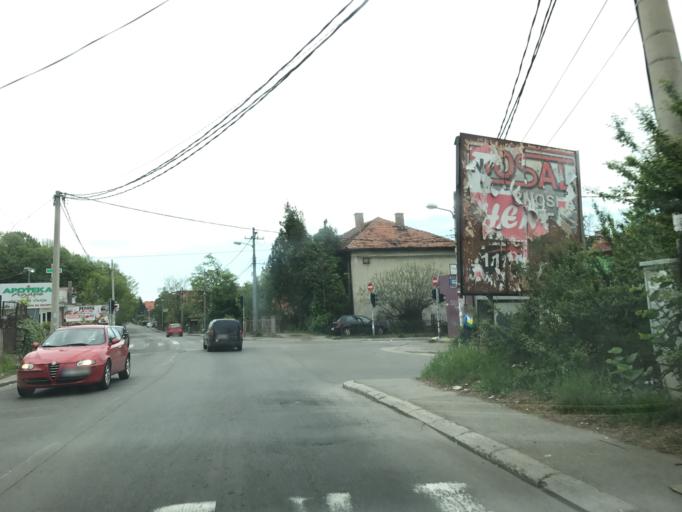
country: RS
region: Central Serbia
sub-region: Belgrade
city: Palilula
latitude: 44.8050
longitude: 20.5178
